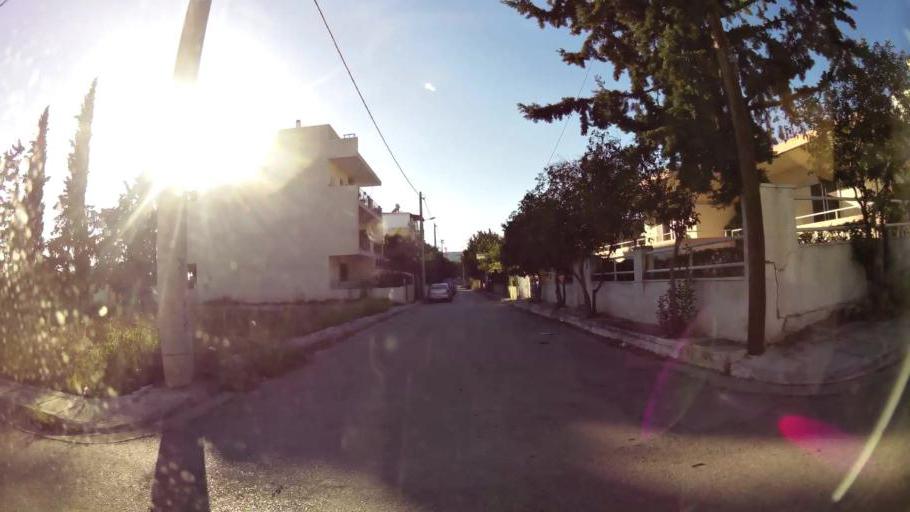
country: GR
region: Attica
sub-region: Nomarchia Anatolikis Attikis
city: Acharnes
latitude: 38.0924
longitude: 23.7232
